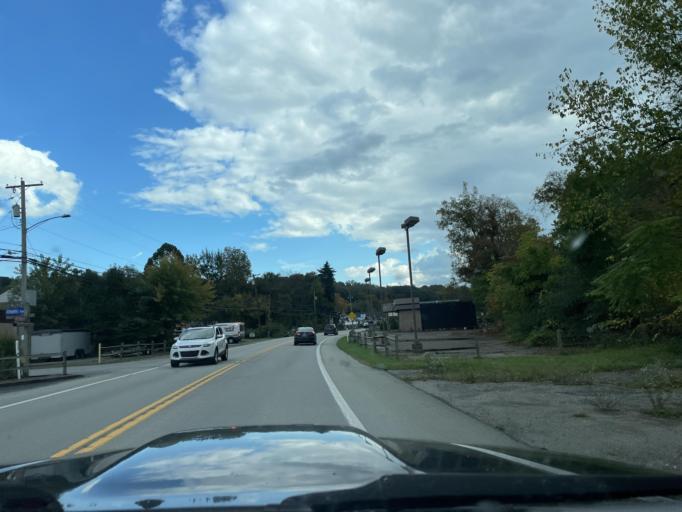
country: US
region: Pennsylvania
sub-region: Westmoreland County
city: Lower Burrell
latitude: 40.5493
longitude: -79.7357
